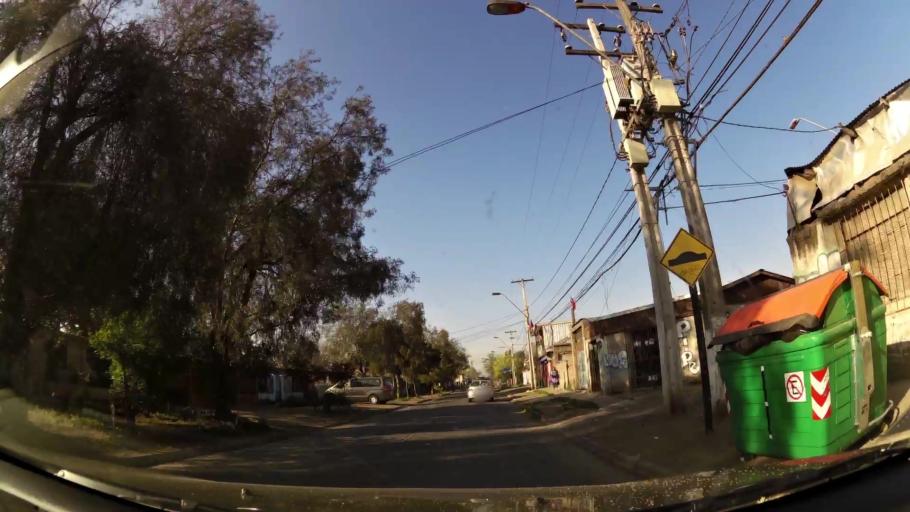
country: CL
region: Santiago Metropolitan
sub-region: Provincia de Santiago
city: Santiago
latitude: -33.3764
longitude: -70.6690
